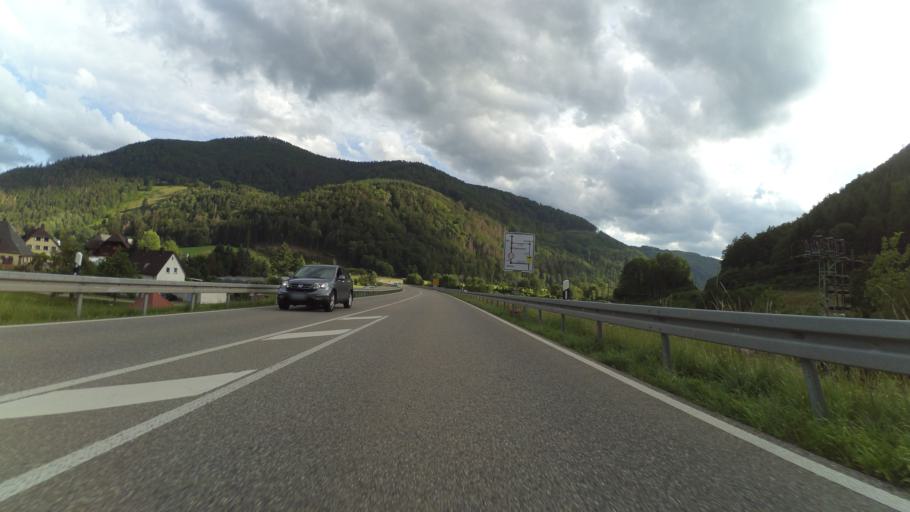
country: DE
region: Baden-Wuerttemberg
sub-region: Freiburg Region
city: Utzenfeld
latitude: 47.8070
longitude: 7.9351
